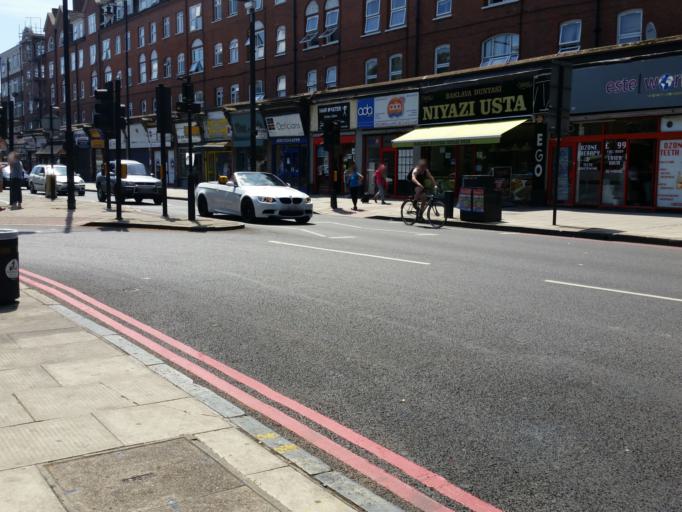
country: GB
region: England
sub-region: Greater London
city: Hackney
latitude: 51.5574
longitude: -0.0747
